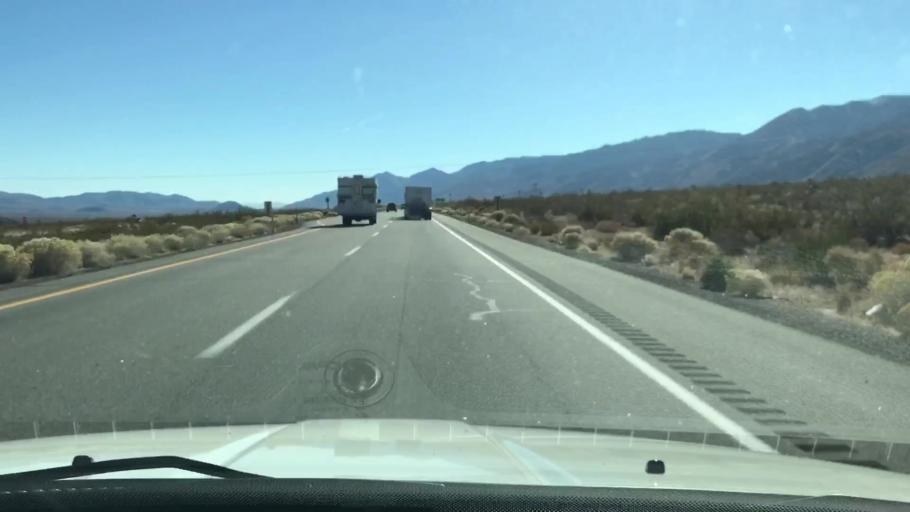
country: US
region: California
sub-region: Inyo County
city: Lone Pine
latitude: 36.1413
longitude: -117.9748
